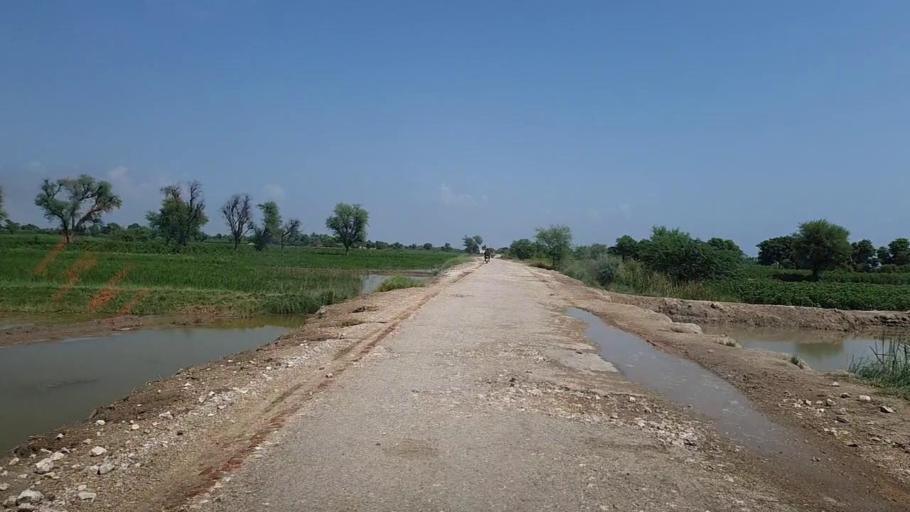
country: PK
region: Sindh
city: Bhiria
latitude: 26.8916
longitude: 68.2264
